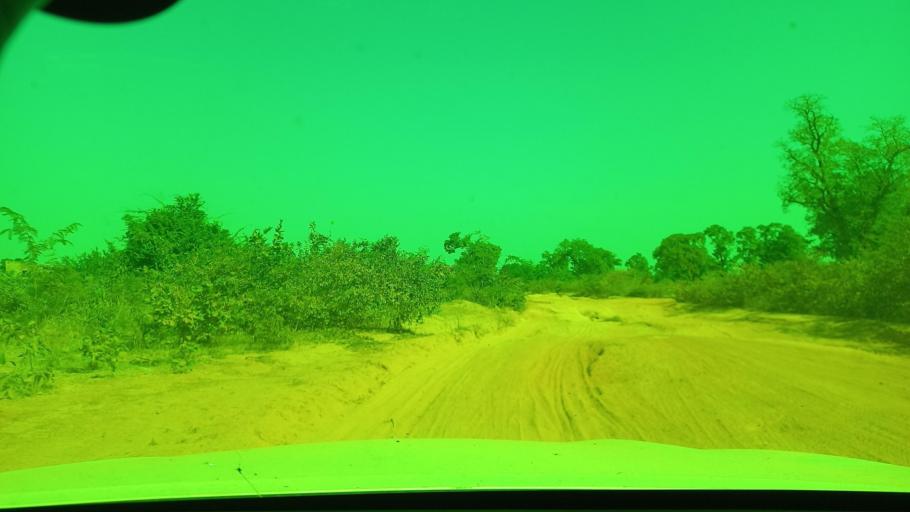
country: ML
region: Bamako
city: Bamako
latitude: 12.3966
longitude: -7.9815
